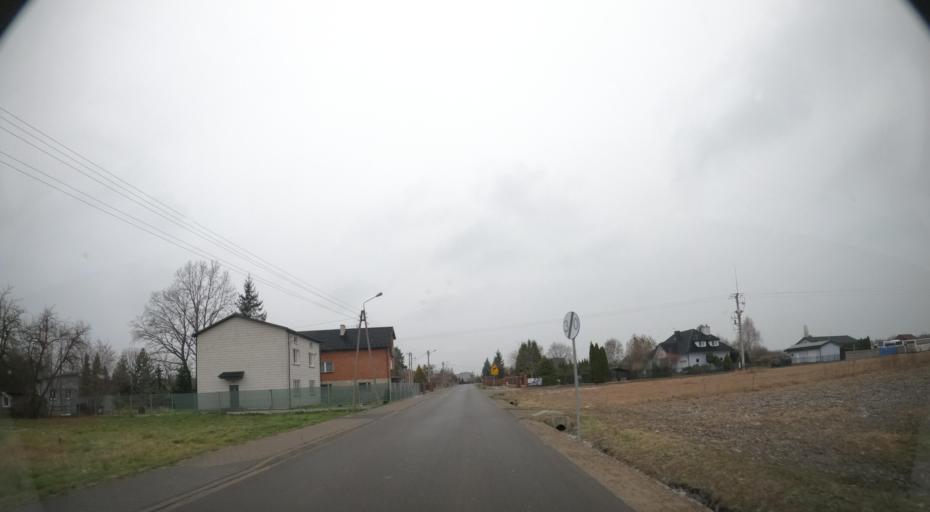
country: PL
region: Masovian Voivodeship
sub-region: Powiat radomski
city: Skaryszew
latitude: 51.3796
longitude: 21.2350
